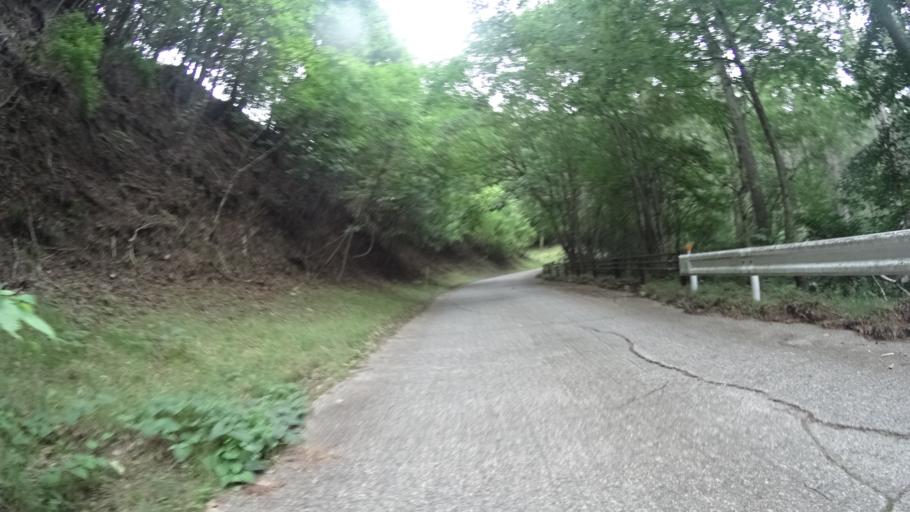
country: JP
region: Yamanashi
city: Kofu-shi
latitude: 35.8524
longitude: 138.5772
